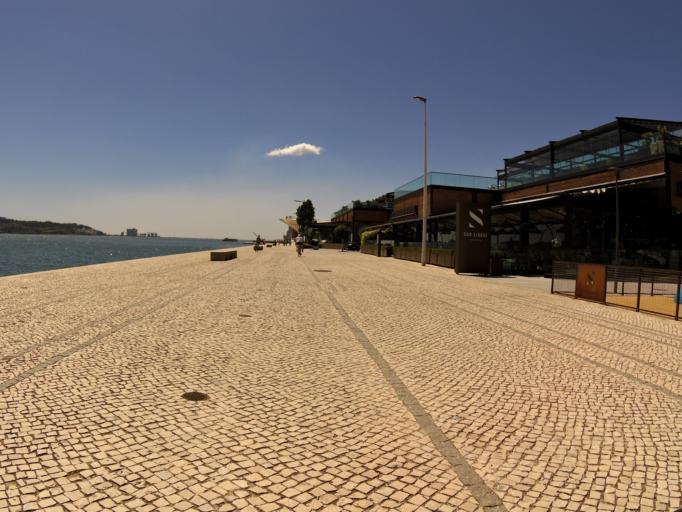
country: PT
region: Setubal
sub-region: Almada
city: Pragal
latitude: 38.6962
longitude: -9.1908
